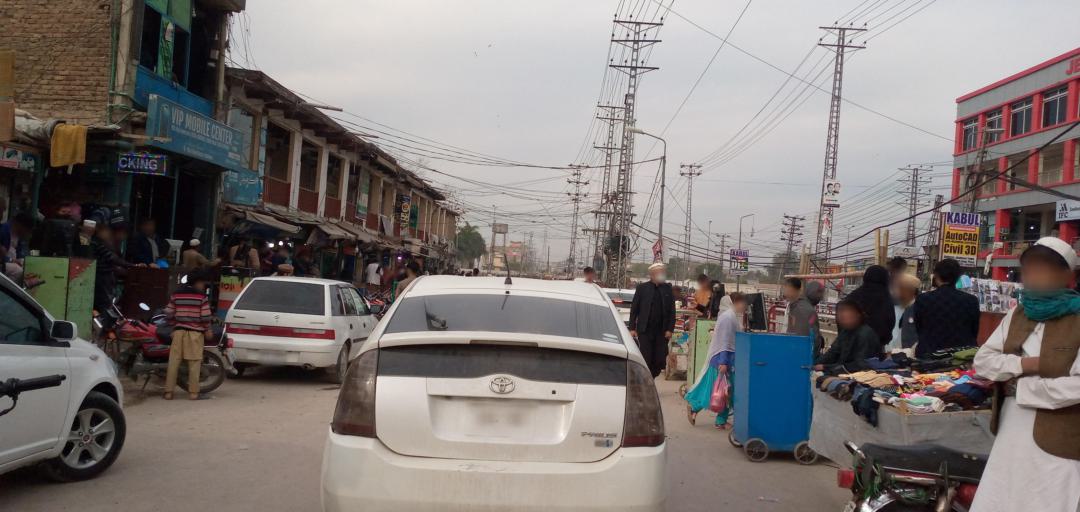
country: PK
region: Khyber Pakhtunkhwa
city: Peshawar
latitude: 33.9967
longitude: 71.4698
